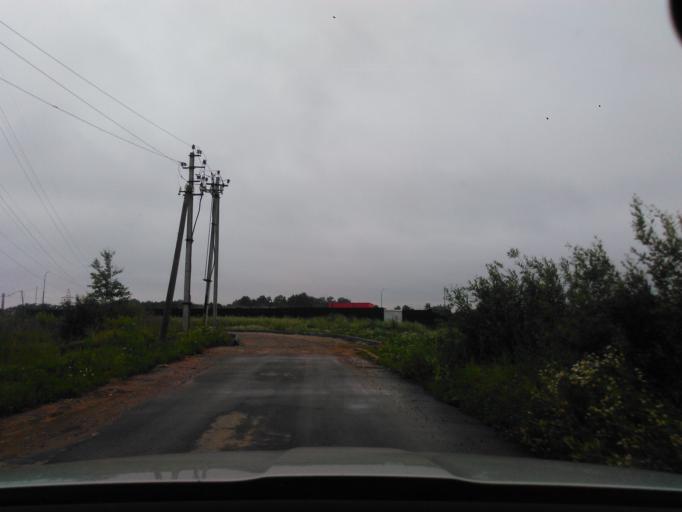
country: RU
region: Moskovskaya
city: Firsanovka
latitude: 55.9393
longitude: 37.2416
